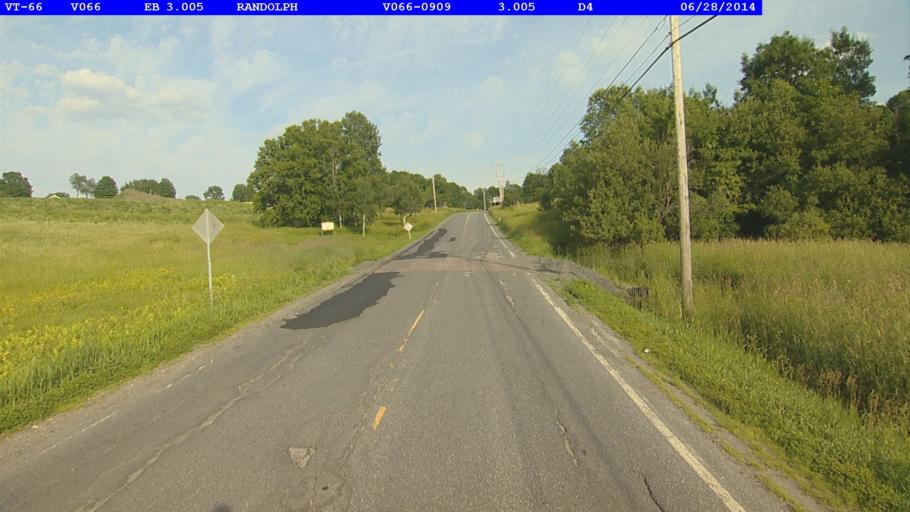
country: US
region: Vermont
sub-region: Orange County
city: Randolph
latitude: 43.9434
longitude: -72.6127
